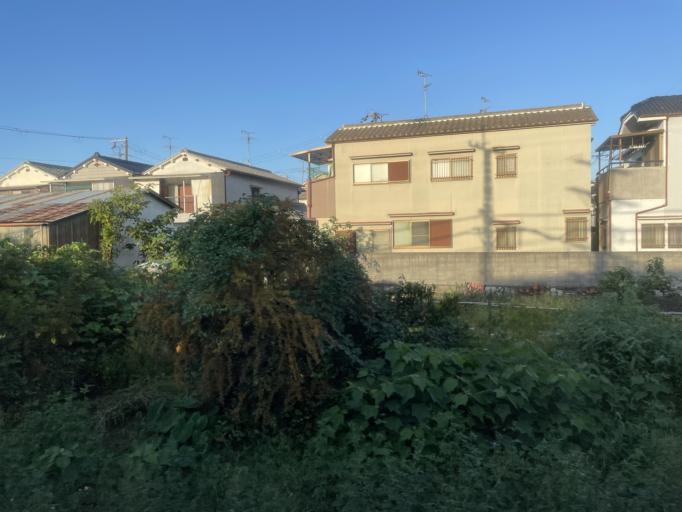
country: JP
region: Osaka
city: Matsubara
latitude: 34.5829
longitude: 135.5369
